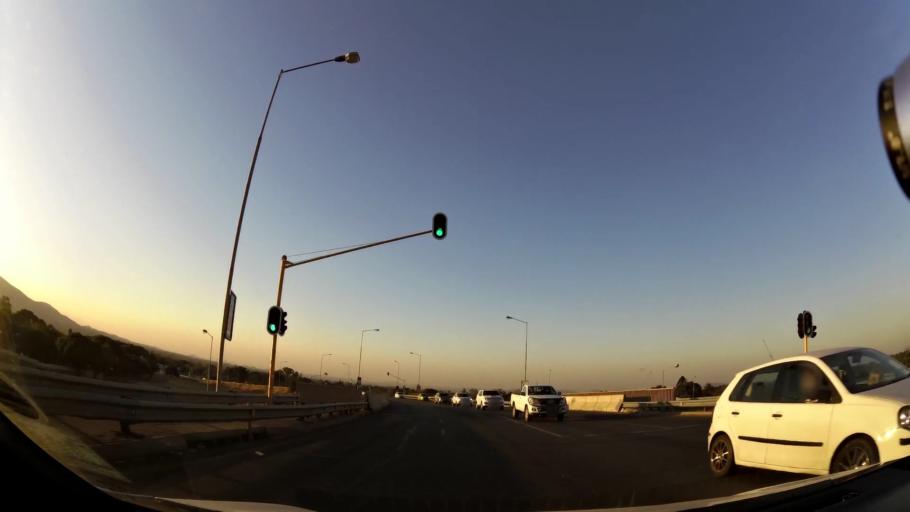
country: ZA
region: North-West
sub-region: Bojanala Platinum District Municipality
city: Rustenburg
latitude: -25.6901
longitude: 27.2262
